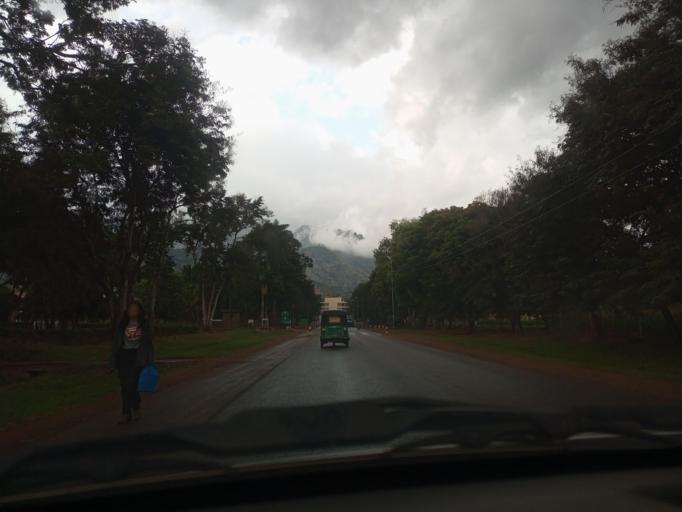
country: TZ
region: Morogoro
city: Morogoro
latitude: -6.8487
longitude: 37.6577
